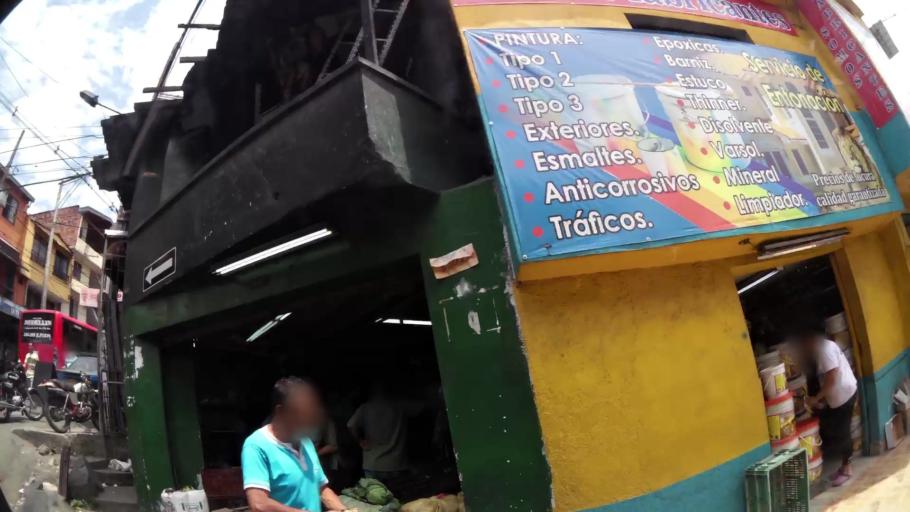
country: CO
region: Antioquia
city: Bello
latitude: 6.3104
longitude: -75.5793
